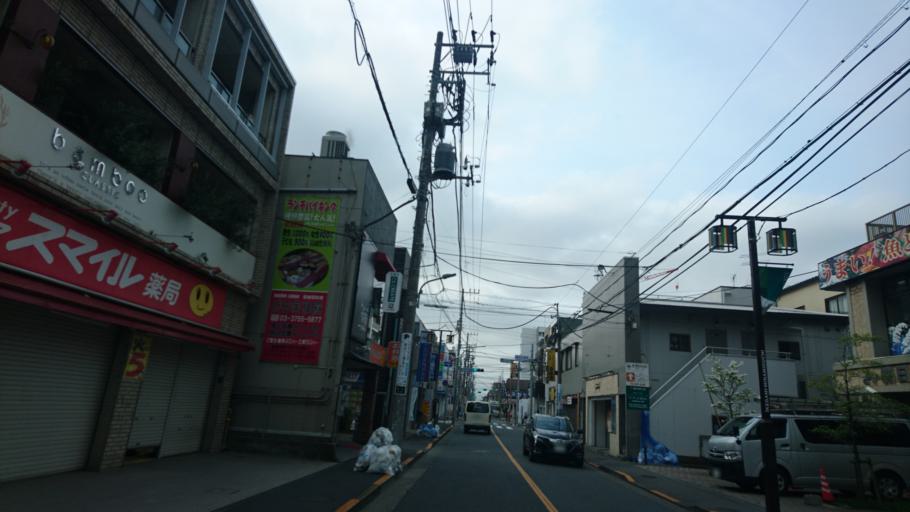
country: JP
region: Kanagawa
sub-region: Kawasaki-shi
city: Kawasaki
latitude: 35.5717
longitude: 139.7037
